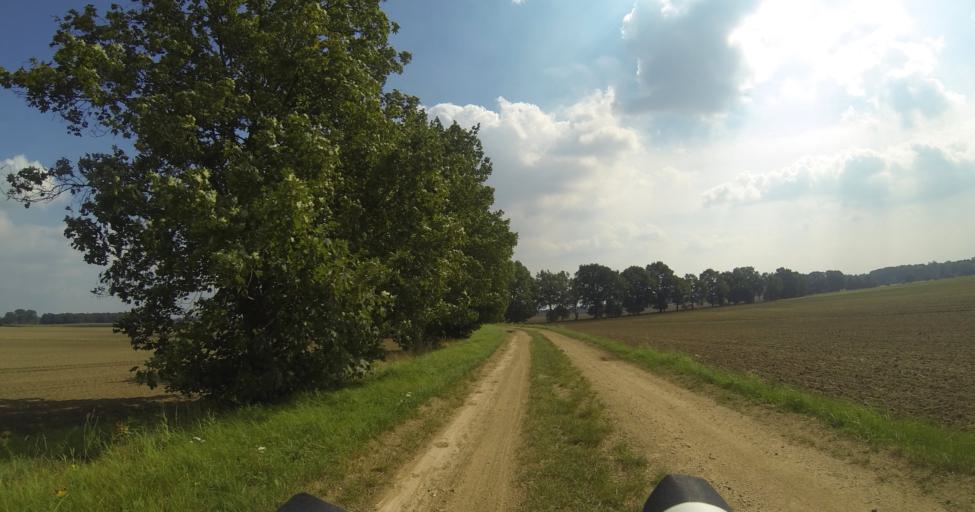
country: DE
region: Saxony
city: Grossenhain
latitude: 51.2615
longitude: 13.5555
